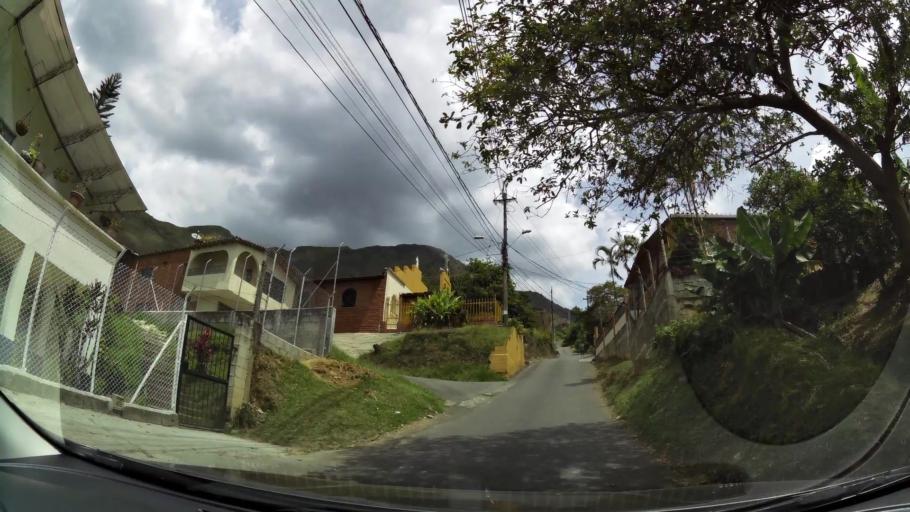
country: CO
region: Antioquia
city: Municipio de Copacabana
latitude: 6.3270
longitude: -75.5001
